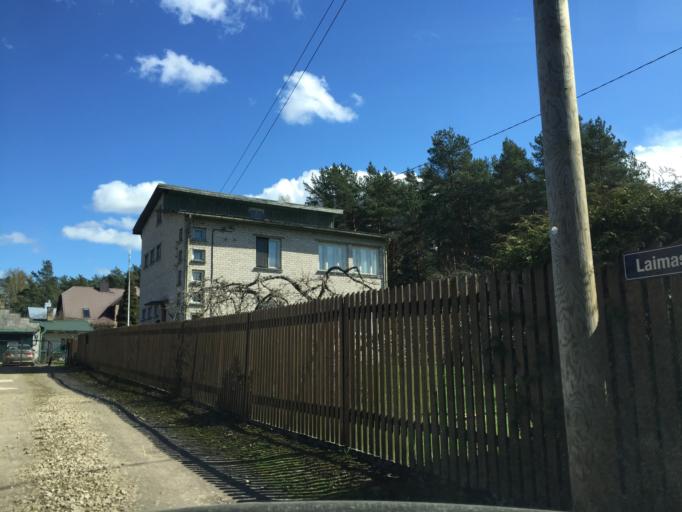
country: LV
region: Riga
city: Bergi
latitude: 56.9957
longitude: 24.2708
